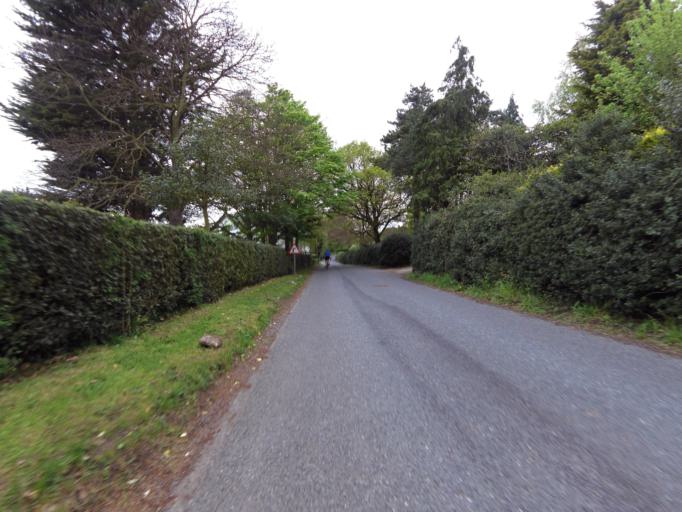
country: GB
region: England
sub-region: Suffolk
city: Kesgrave
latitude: 52.0113
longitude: 1.2344
